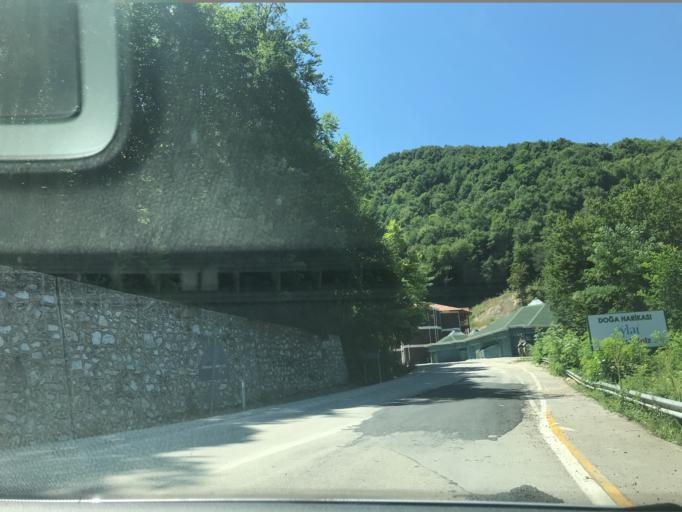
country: TR
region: Bursa
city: Tahtakopru
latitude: 39.9286
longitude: 29.5881
